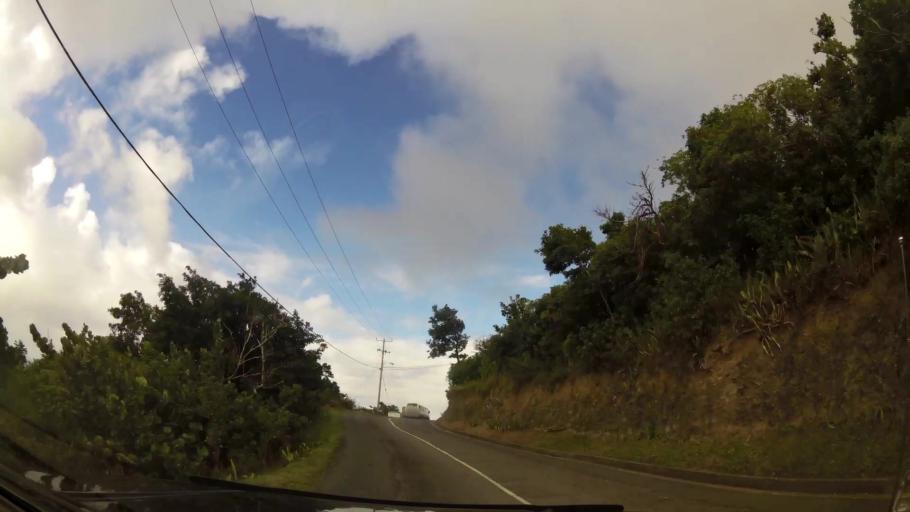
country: MS
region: Saint Peter
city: Saint Peters
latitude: 16.7761
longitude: -62.2105
